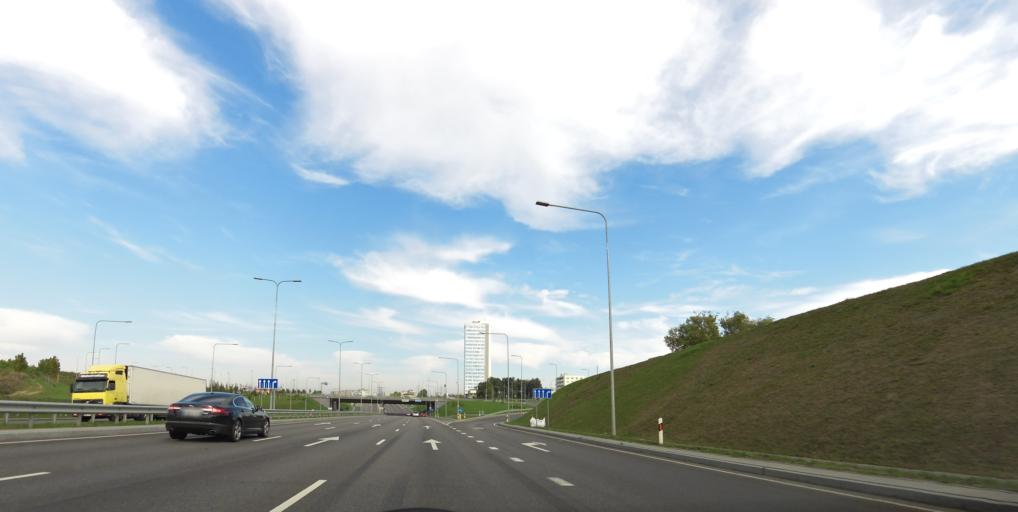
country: LT
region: Vilnius County
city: Justiniskes
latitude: 54.6979
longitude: 25.2078
